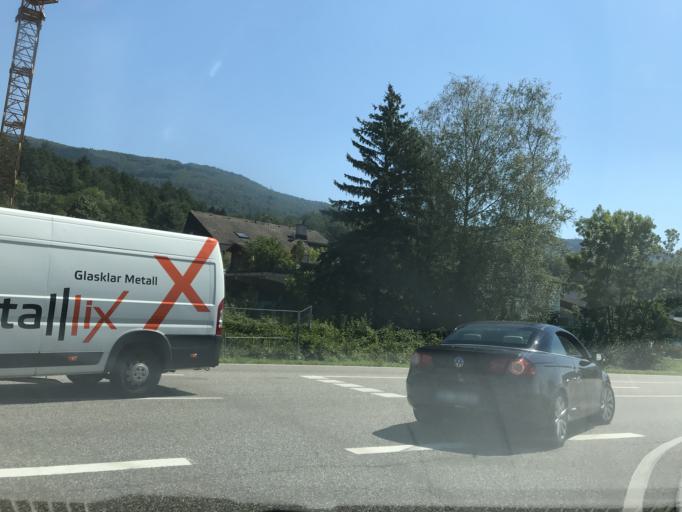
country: DE
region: Baden-Wuerttemberg
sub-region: Freiburg Region
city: Wehr
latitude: 47.6120
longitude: 7.9108
